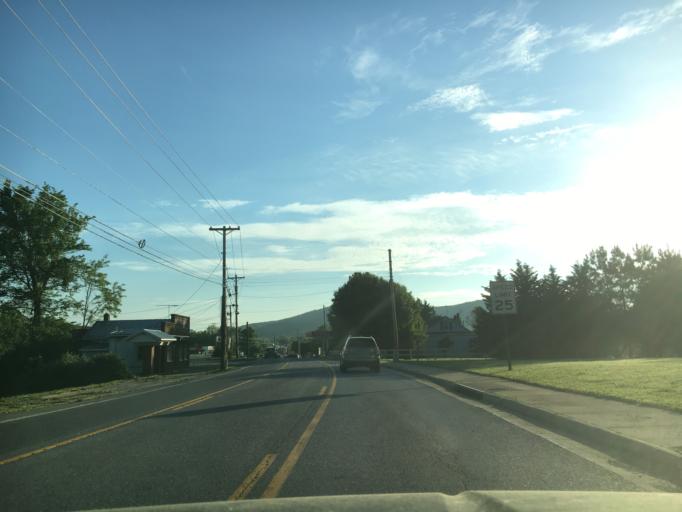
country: US
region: Virginia
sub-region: Campbell County
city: Rustburg
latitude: 37.2718
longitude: -79.1067
